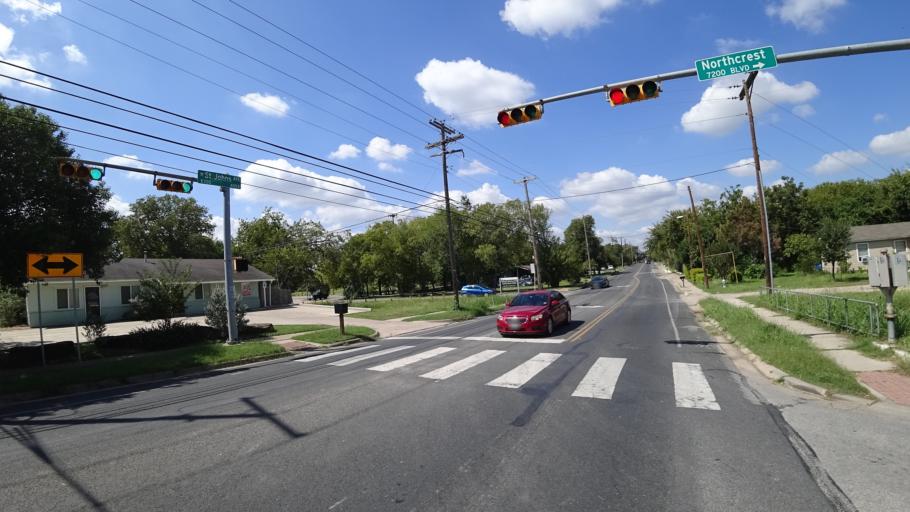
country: US
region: Texas
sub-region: Travis County
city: Austin
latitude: 30.3367
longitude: -97.7119
